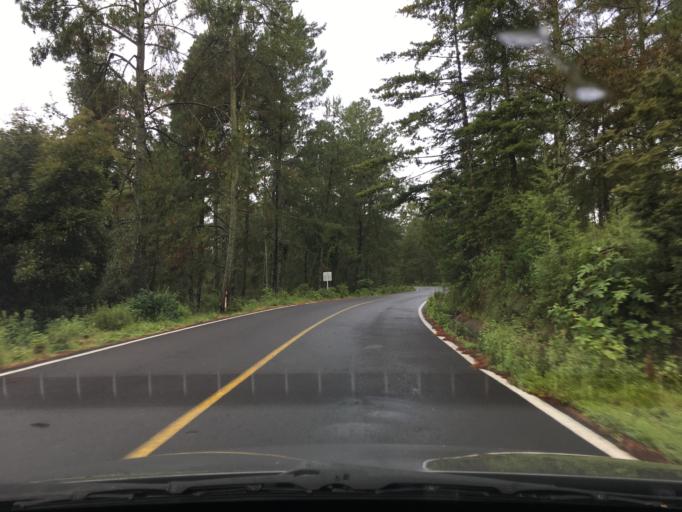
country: MX
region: Michoacan
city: Nuevo San Juan Parangaricutiro
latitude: 19.4434
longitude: -102.1665
